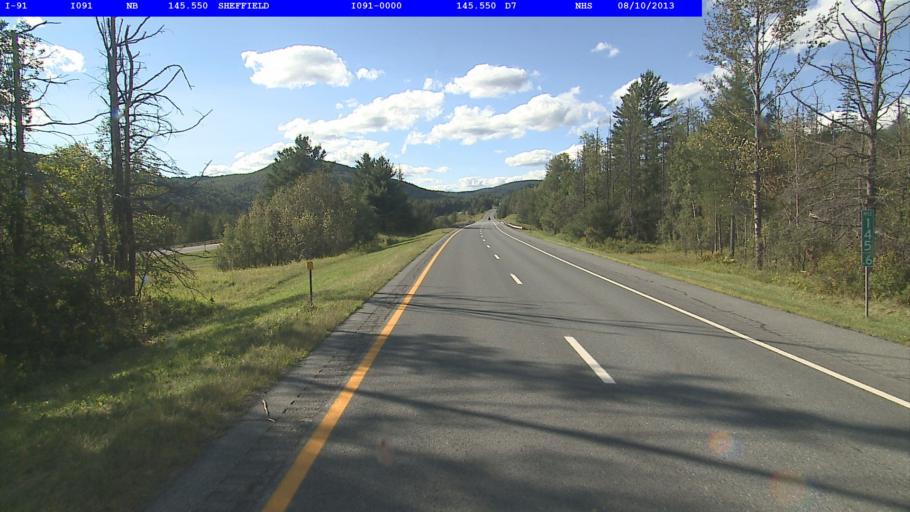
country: US
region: Vermont
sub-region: Caledonia County
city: Lyndonville
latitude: 44.6040
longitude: -72.1099
